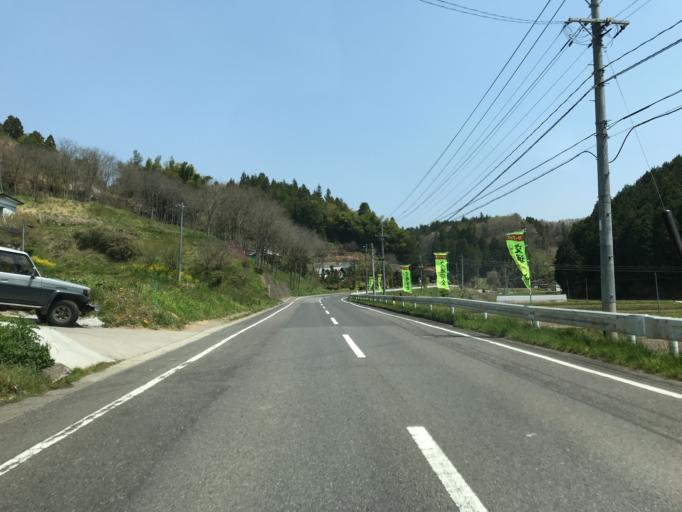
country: JP
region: Fukushima
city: Ishikawa
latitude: 37.0666
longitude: 140.4398
